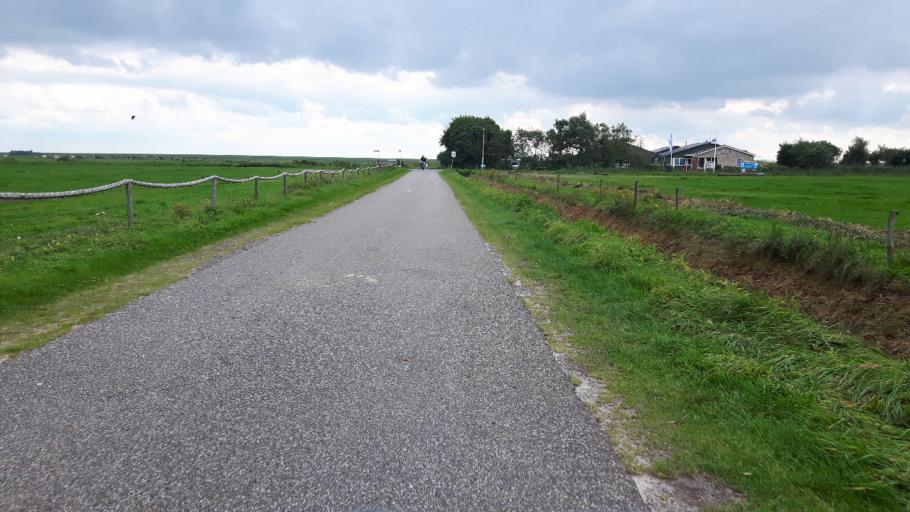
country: NL
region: Friesland
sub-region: Gemeente Ameland
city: Nes
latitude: 53.4507
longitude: 5.8181
